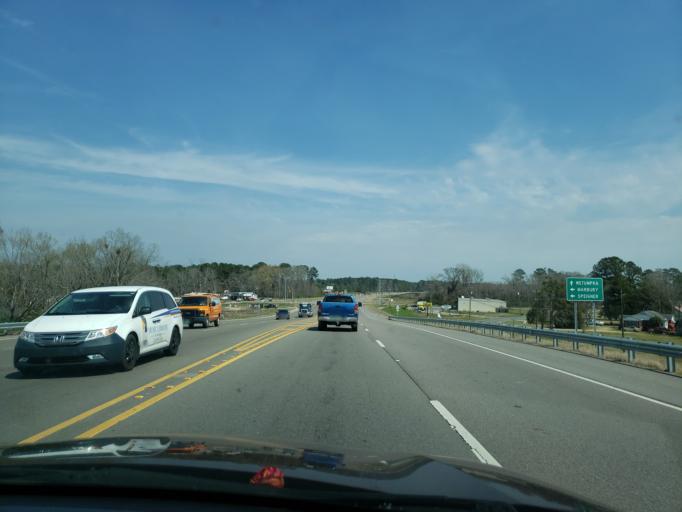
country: US
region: Alabama
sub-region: Elmore County
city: Elmore
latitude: 32.5390
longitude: -86.3144
